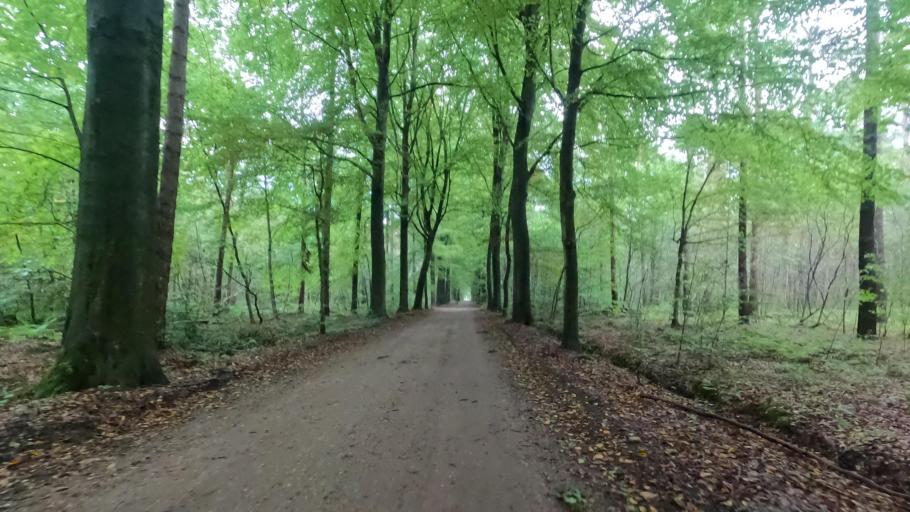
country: BE
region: Flanders
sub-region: Provincie Antwerpen
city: Schilde
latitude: 51.2330
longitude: 4.5993
